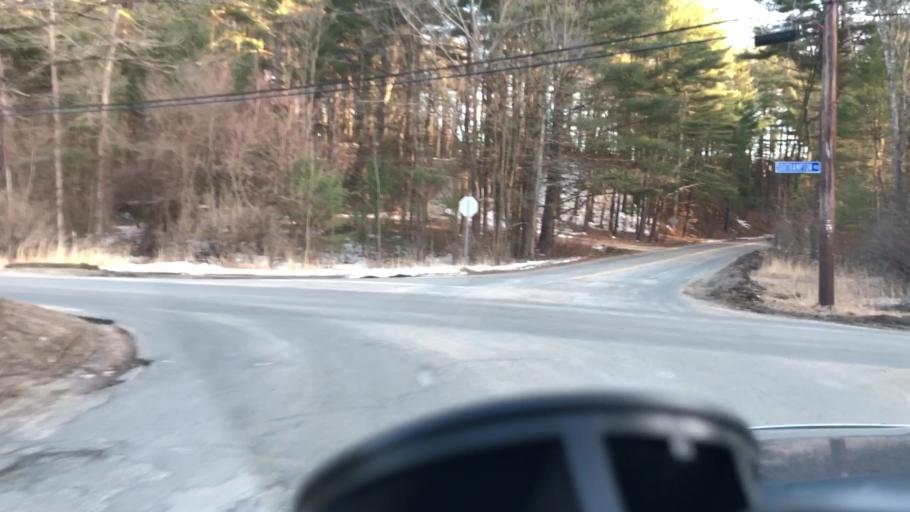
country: US
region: Massachusetts
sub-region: Hampshire County
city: Southampton
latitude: 42.2106
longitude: -72.6796
